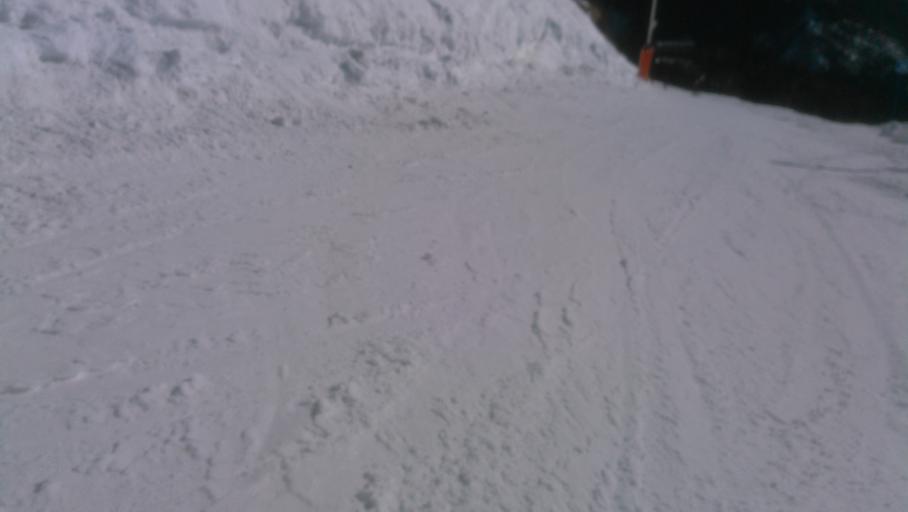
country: SK
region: Banskobystricky
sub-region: Okres Banska Bystrica
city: Brezno
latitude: 48.9282
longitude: 19.5979
